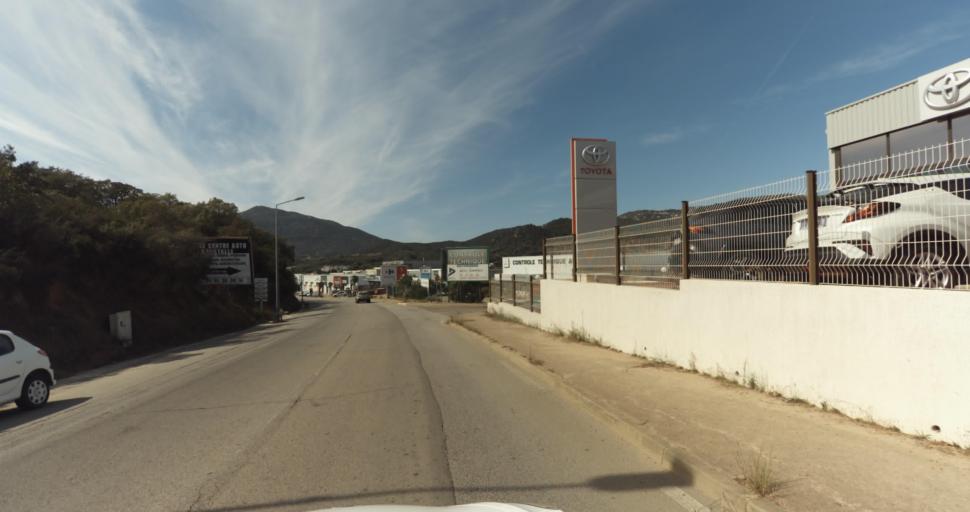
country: FR
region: Corsica
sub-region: Departement de la Corse-du-Sud
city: Ajaccio
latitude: 41.9463
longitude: 8.7678
